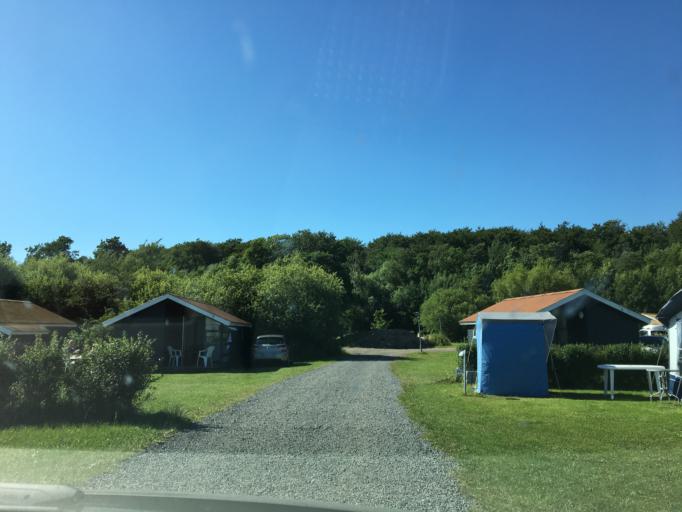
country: DK
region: South Denmark
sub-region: Svendborg Kommune
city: Thuro By
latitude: 55.0441
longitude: 10.7087
